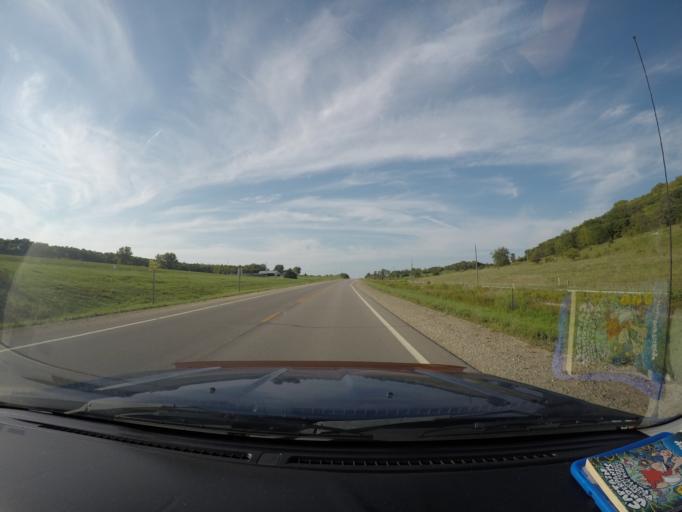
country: US
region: Kansas
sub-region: Atchison County
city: Atchison
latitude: 39.5042
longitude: -95.1326
